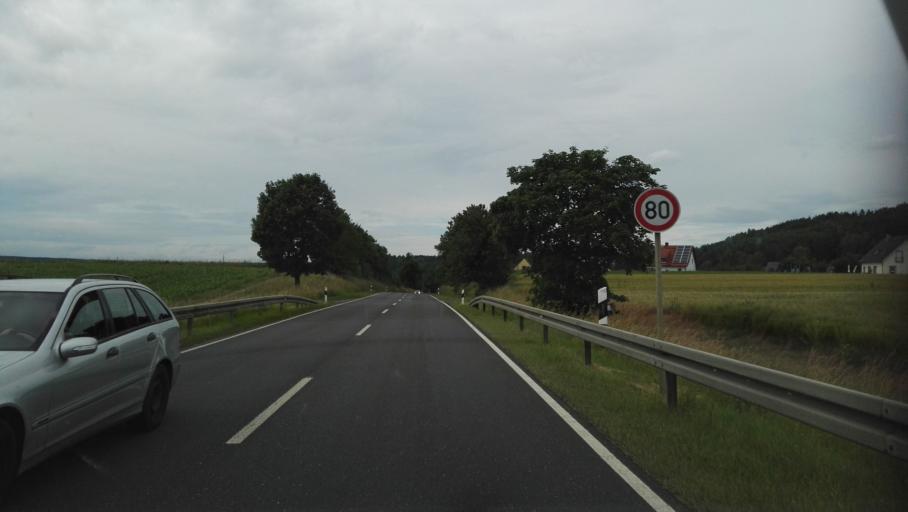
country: DE
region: Bavaria
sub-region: Upper Franconia
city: Plankenfels
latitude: 49.8932
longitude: 11.3344
